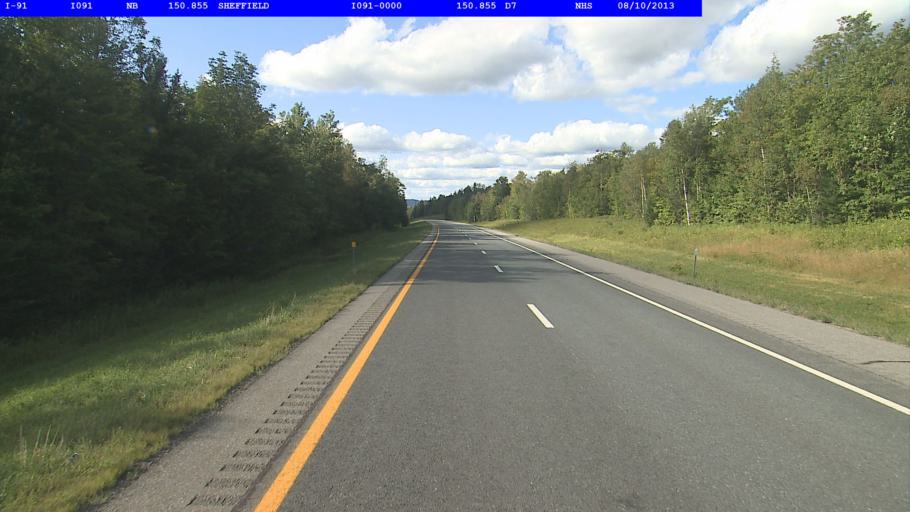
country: US
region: Vermont
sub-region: Caledonia County
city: Lyndonville
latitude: 44.6768
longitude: -72.1315
